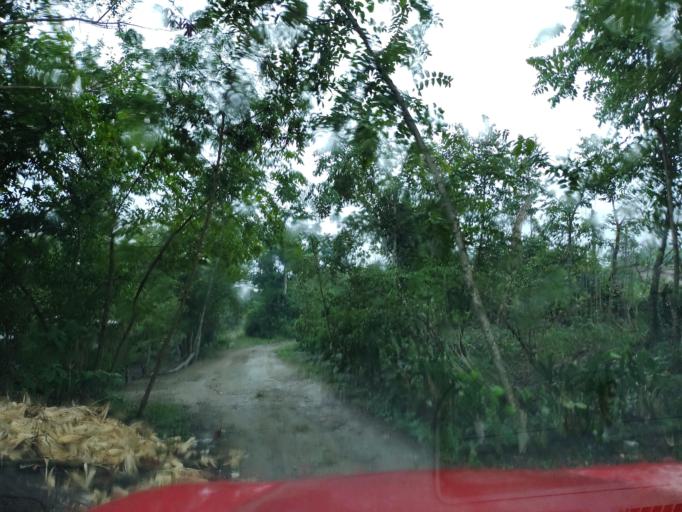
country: MX
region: Veracruz
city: Agua Dulce
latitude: 20.3354
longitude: -97.3172
